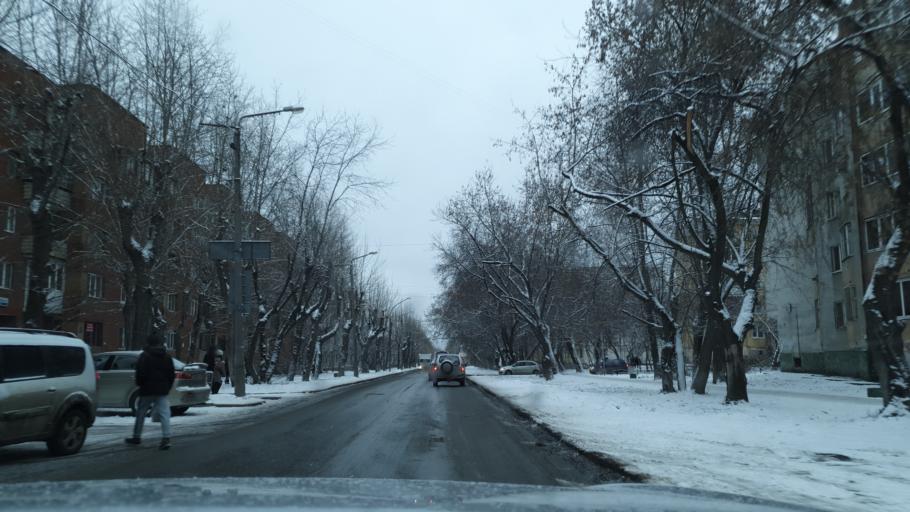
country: RU
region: Sverdlovsk
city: Istok
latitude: 56.7525
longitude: 60.7088
